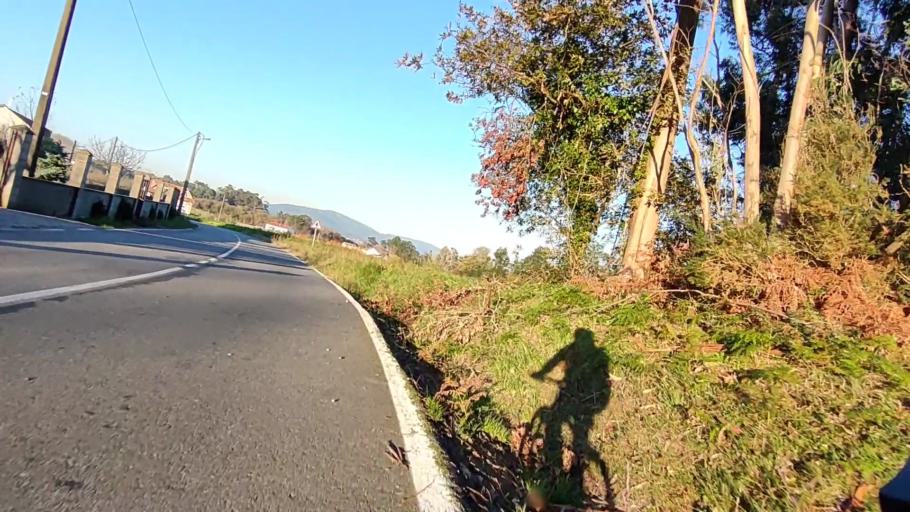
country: ES
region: Galicia
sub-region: Provincia da Coruna
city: Rianxo
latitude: 42.6336
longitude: -8.8581
